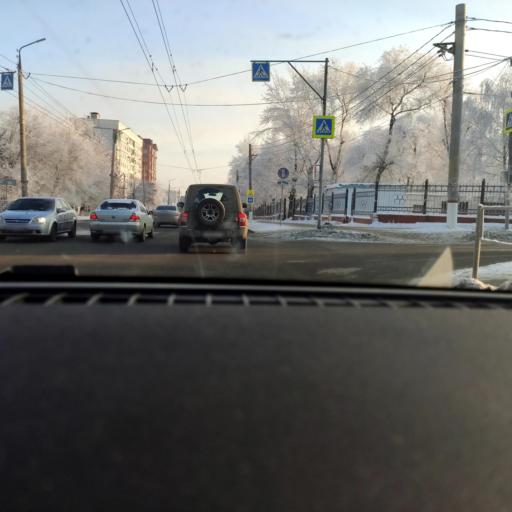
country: RU
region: Samara
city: Novokuybyshevsk
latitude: 53.0947
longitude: 49.9748
